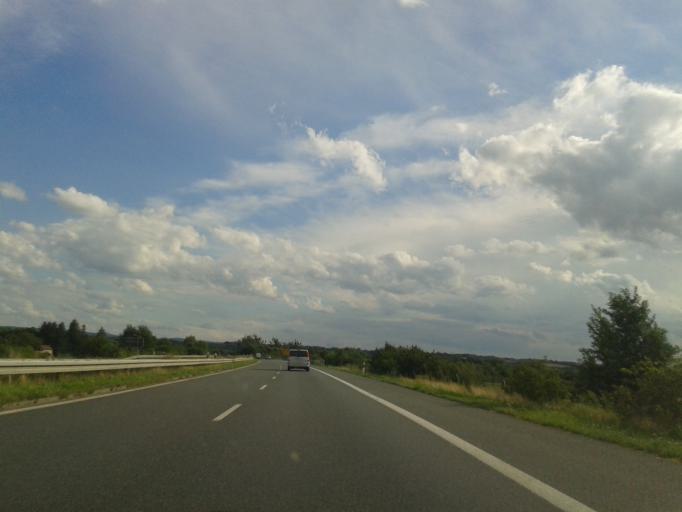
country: DE
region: Saxony
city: Pirna
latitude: 50.9782
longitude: 13.9160
